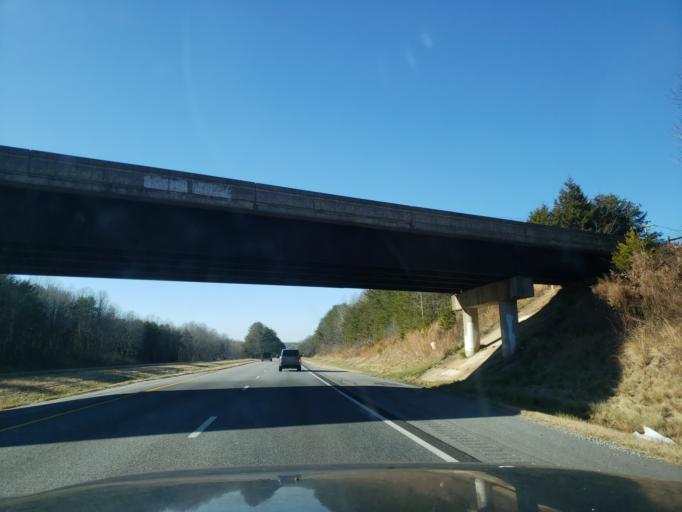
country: US
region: North Carolina
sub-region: Davidson County
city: Wallburg
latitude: 36.0312
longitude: -80.0729
